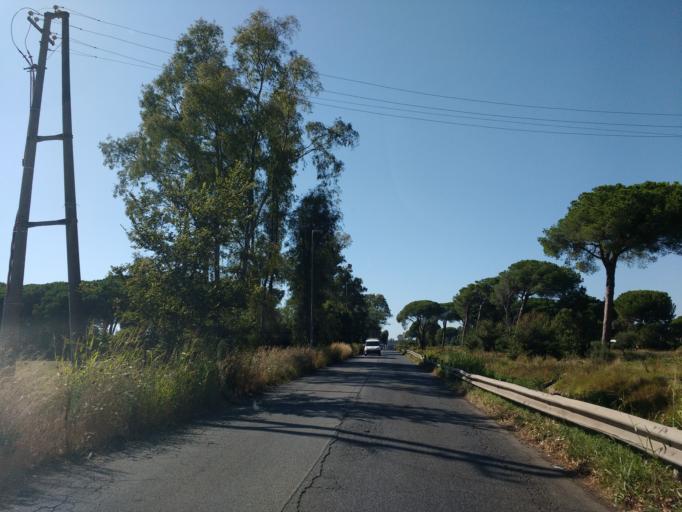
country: IT
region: Latium
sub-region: Citta metropolitana di Roma Capitale
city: Acilia-Castel Fusano-Ostia Antica
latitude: 41.7380
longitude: 12.3439
